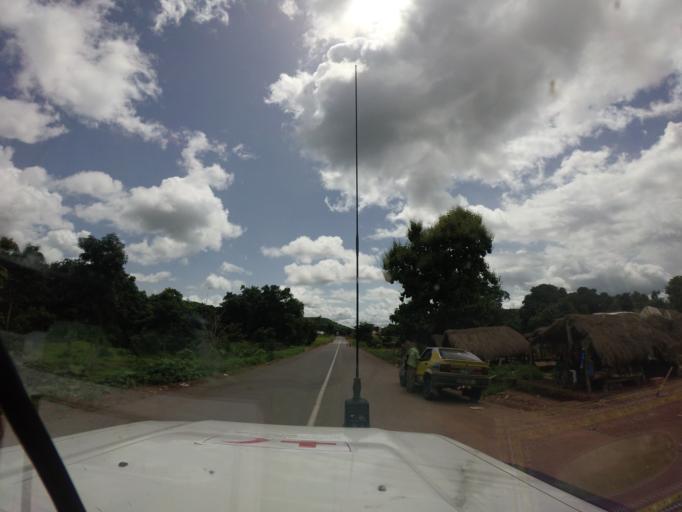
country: SL
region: Northern Province
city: Bindi
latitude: 10.1799
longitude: -11.7249
